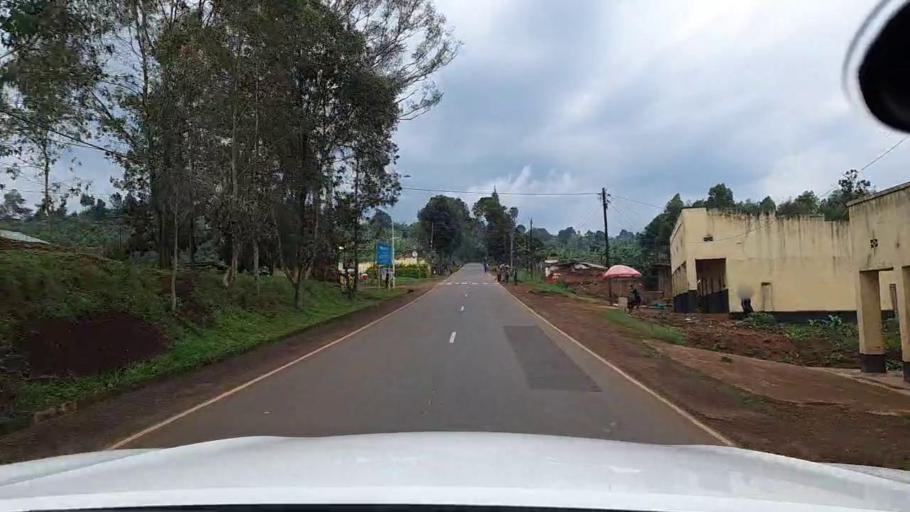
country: RW
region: Western Province
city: Cyangugu
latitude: -2.5377
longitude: 28.8956
